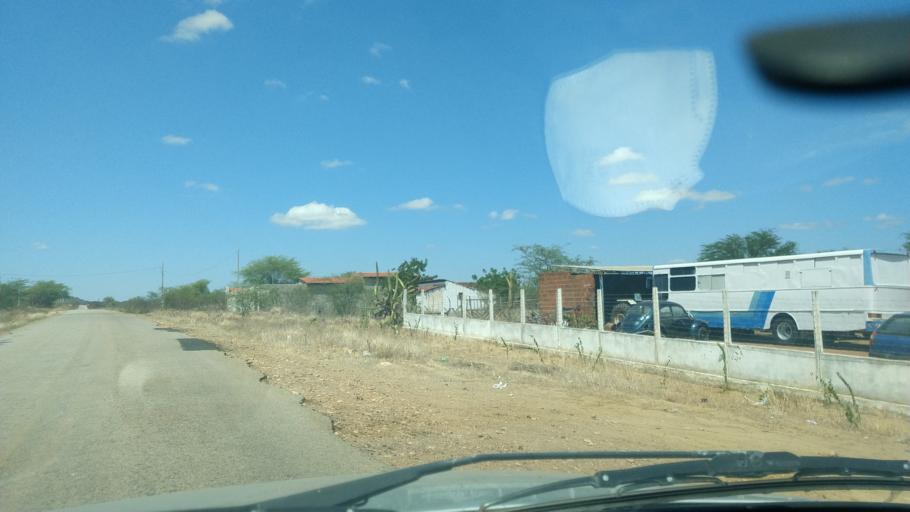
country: BR
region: Rio Grande do Norte
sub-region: Sao Tome
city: Sao Tome
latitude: -5.9694
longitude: -35.9272
